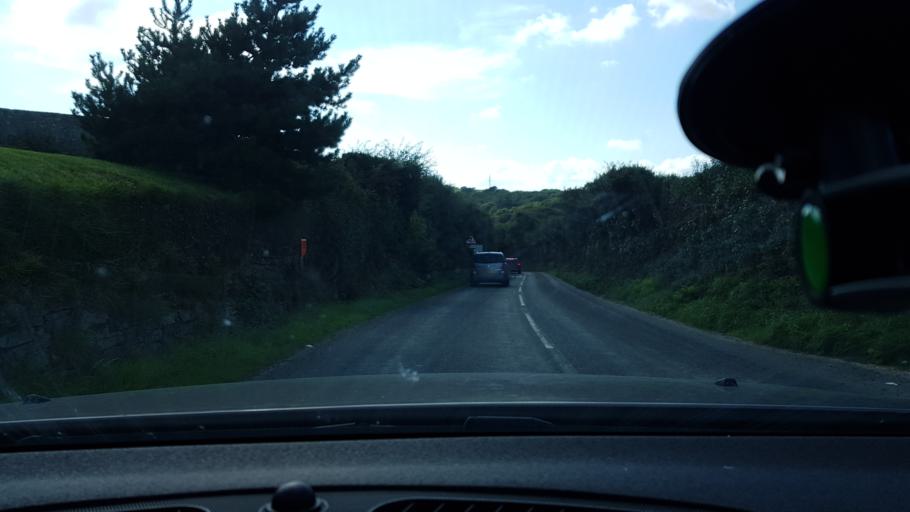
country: GB
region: England
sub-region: Cornwall
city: Tintagel
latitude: 50.6707
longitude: -4.7251
